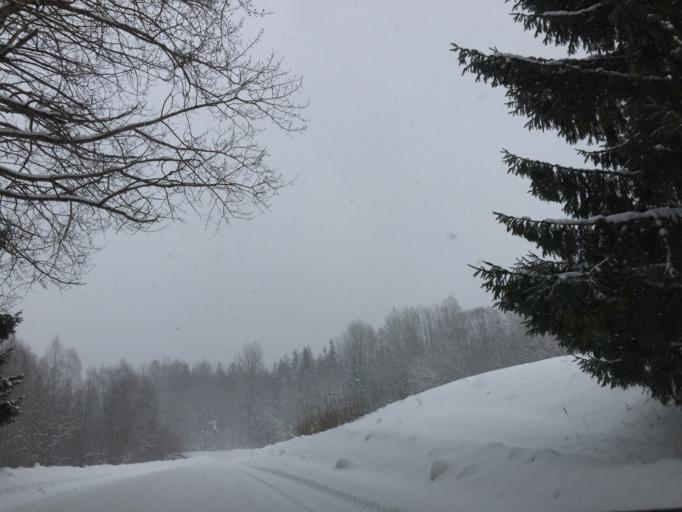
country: LV
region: Amatas Novads
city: Drabesi
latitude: 57.0841
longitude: 25.3666
